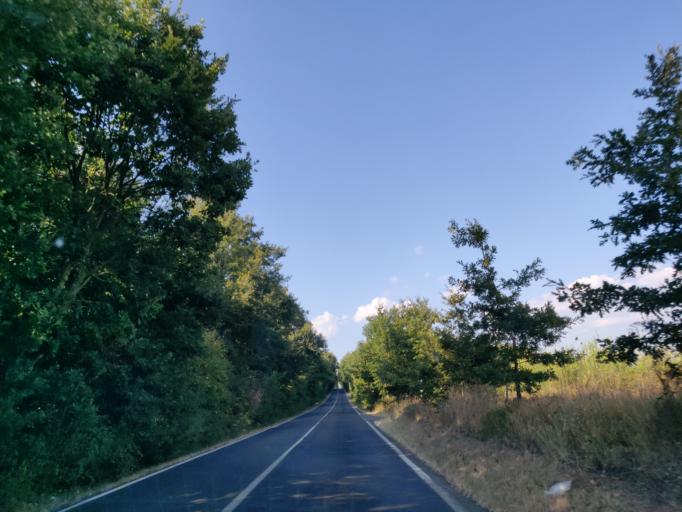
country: IT
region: Latium
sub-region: Provincia di Viterbo
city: Latera
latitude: 42.5994
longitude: 11.8405
